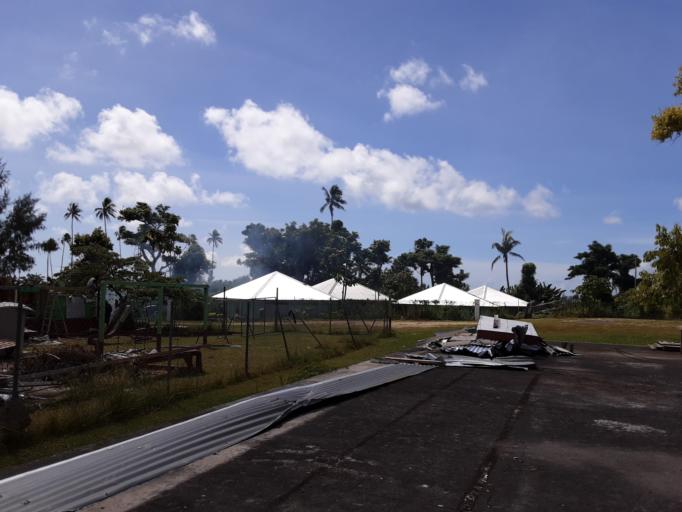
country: VU
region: Sanma
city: Luganville
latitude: -15.5097
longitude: 167.1906
